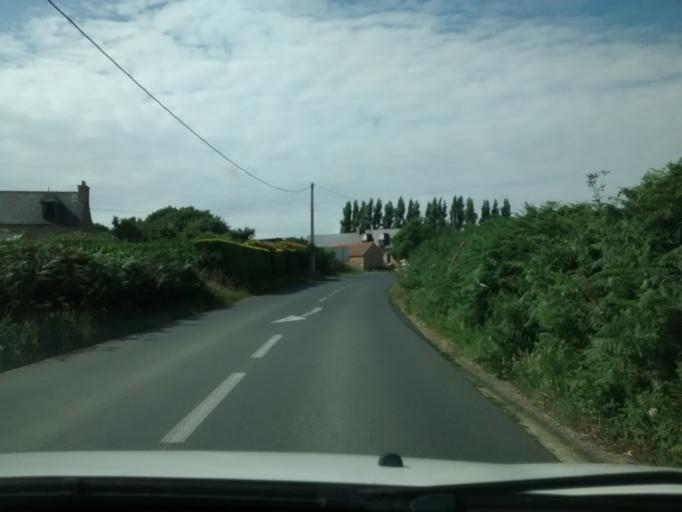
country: FR
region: Brittany
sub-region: Departement des Cotes-d'Armor
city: Penvenan
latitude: 48.7964
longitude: -3.2893
